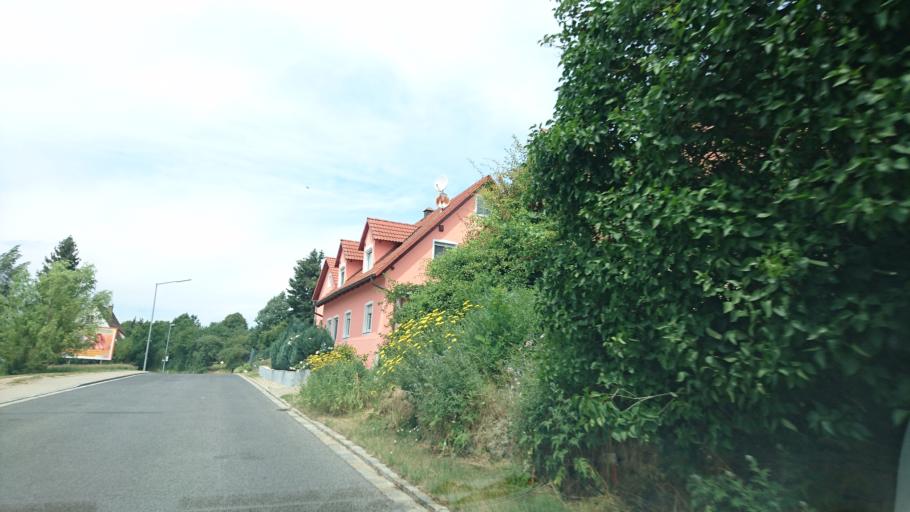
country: DE
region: Bavaria
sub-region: Regierungsbezirk Mittelfranken
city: Thalmassing
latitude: 49.1093
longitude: 11.1826
